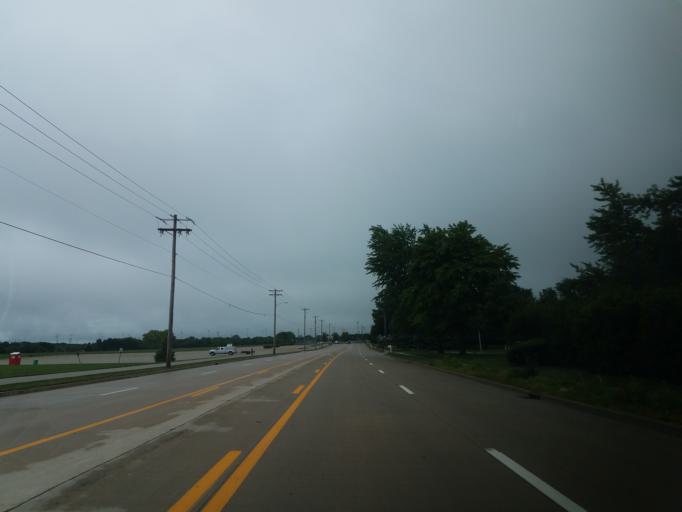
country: US
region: Illinois
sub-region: McLean County
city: Bloomington
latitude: 40.4499
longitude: -88.9970
